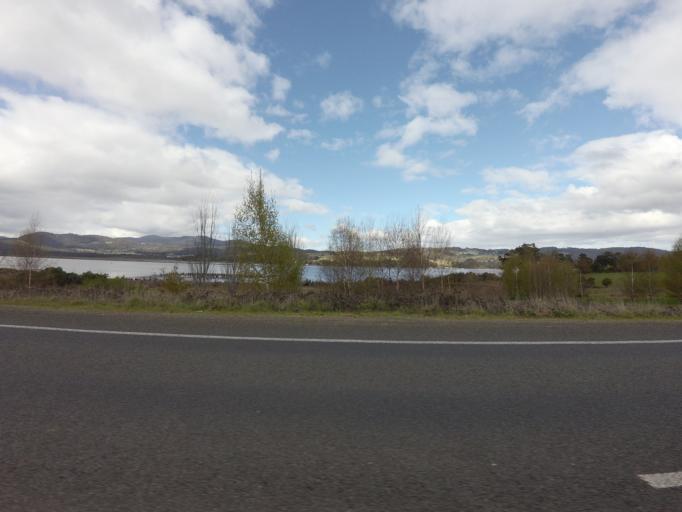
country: AU
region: Tasmania
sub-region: Huon Valley
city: Franklin
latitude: -43.1218
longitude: 146.9898
